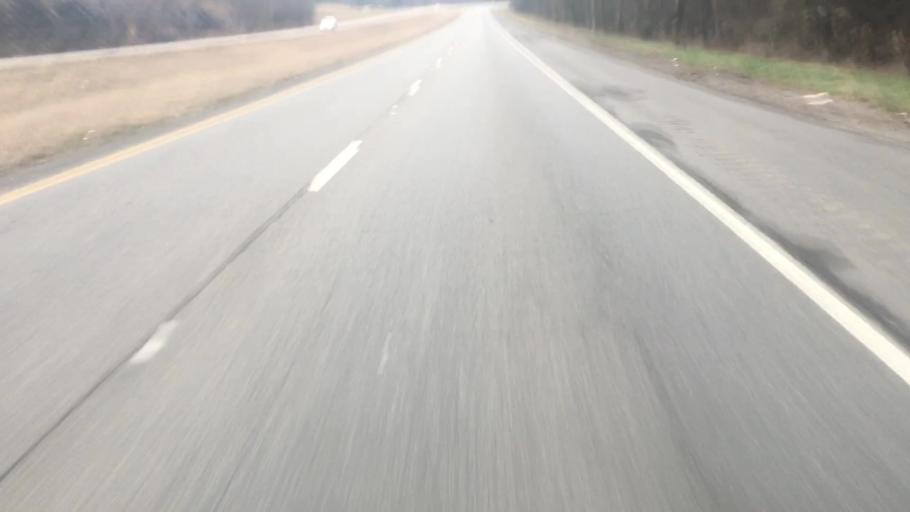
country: US
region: Alabama
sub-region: Walker County
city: Sumiton
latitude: 33.7765
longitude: -87.0793
